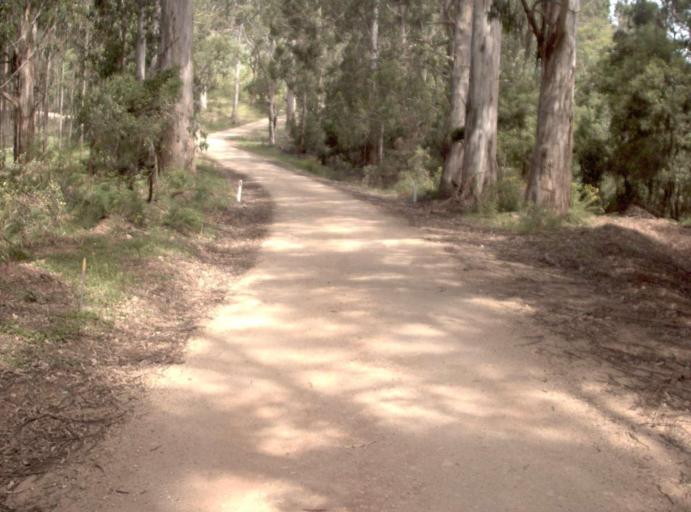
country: AU
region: Victoria
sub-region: East Gippsland
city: Lakes Entrance
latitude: -37.6220
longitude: 148.6918
